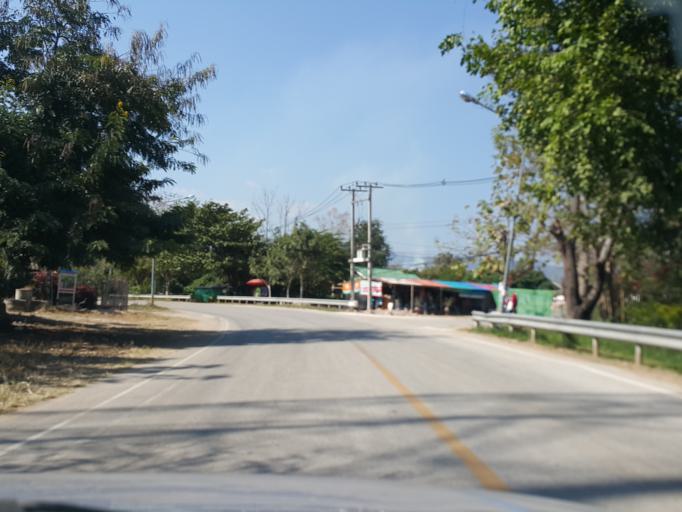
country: TH
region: Chiang Mai
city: Mae Wang
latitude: 18.6147
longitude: 98.7791
